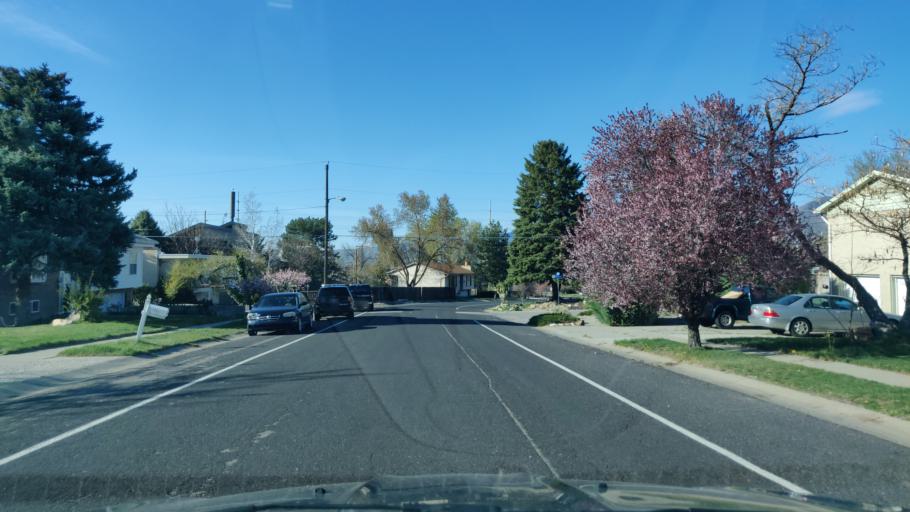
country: US
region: Utah
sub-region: Salt Lake County
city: Little Cottonwood Creek Valley
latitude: 40.6221
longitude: -111.8330
